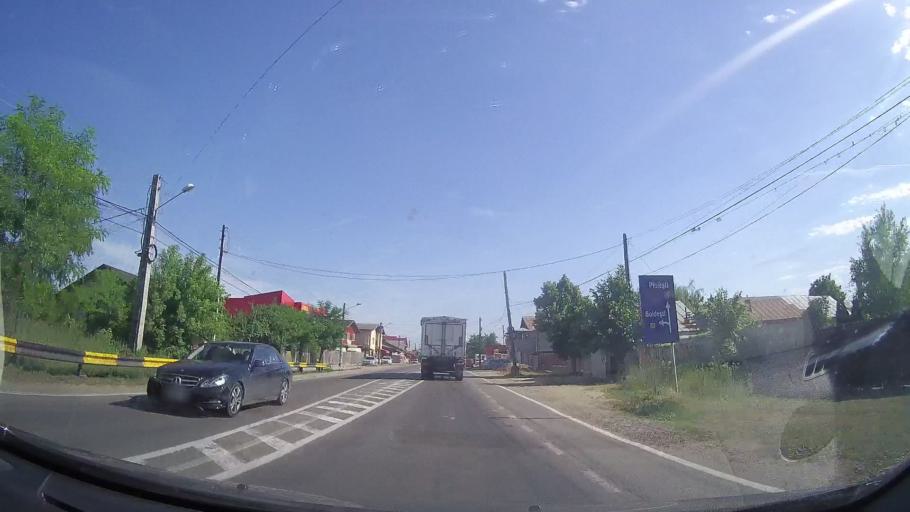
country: RO
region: Prahova
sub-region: Comuna Lipanesti
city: Sipotu
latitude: 45.0309
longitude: 26.0181
